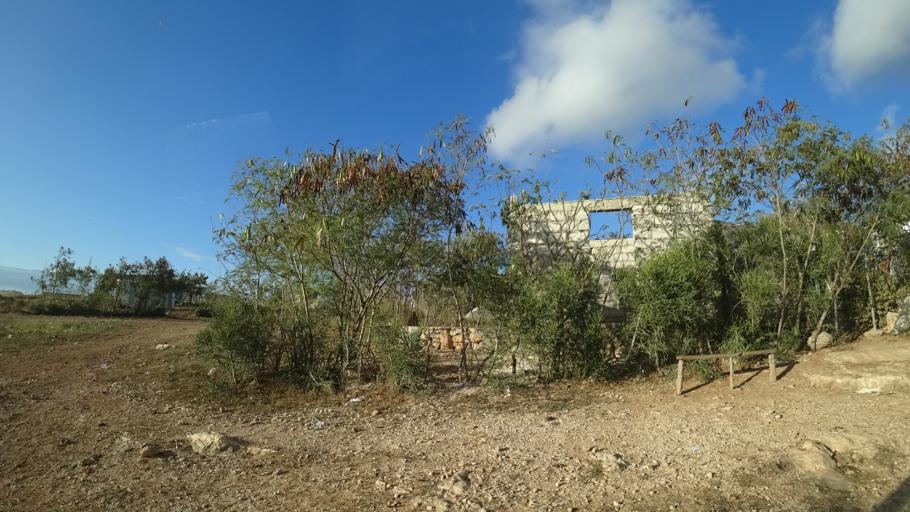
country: HT
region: Ouest
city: Croix des Bouquets
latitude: 18.6695
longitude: -72.2724
